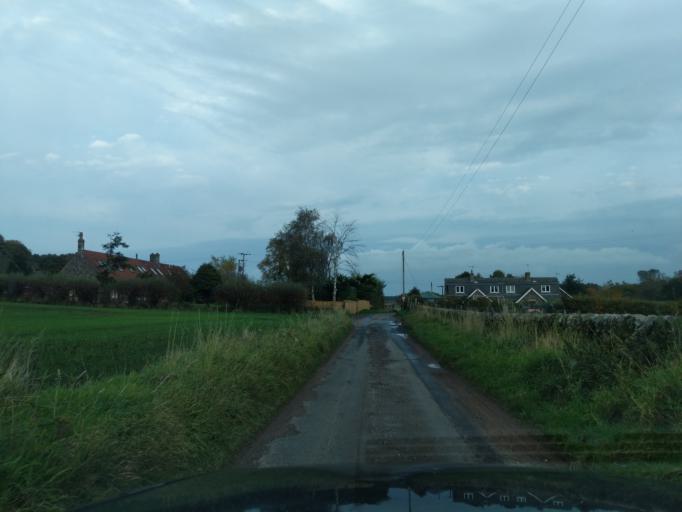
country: GB
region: Scotland
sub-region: Fife
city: Tayport
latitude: 56.4244
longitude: -2.8987
